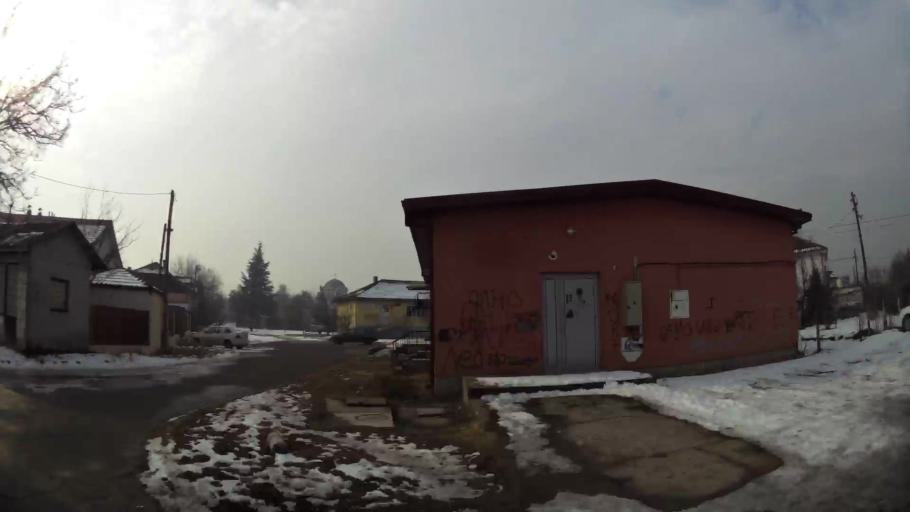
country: MK
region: Kisela Voda
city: Kisela Voda
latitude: 41.9958
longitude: 21.5043
